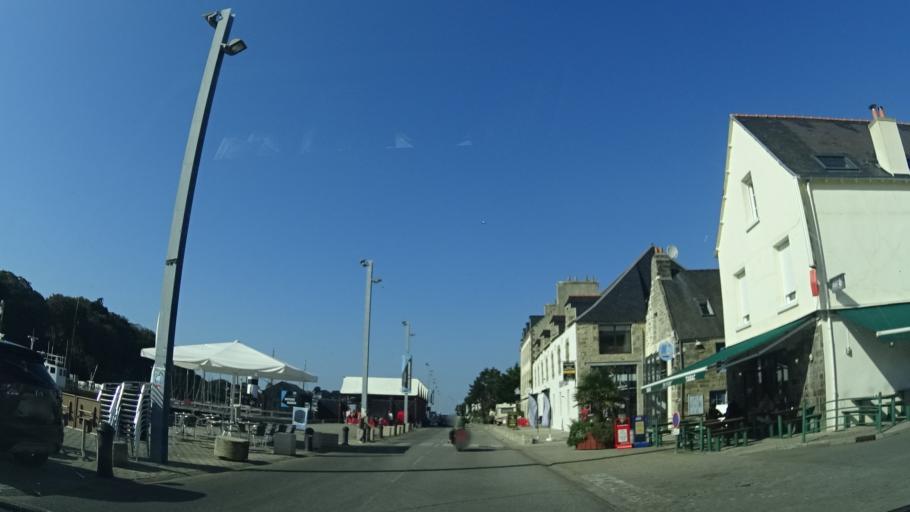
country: FR
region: Brittany
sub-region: Departement du Finistere
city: Douarnenez
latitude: 48.0926
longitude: -4.3335
